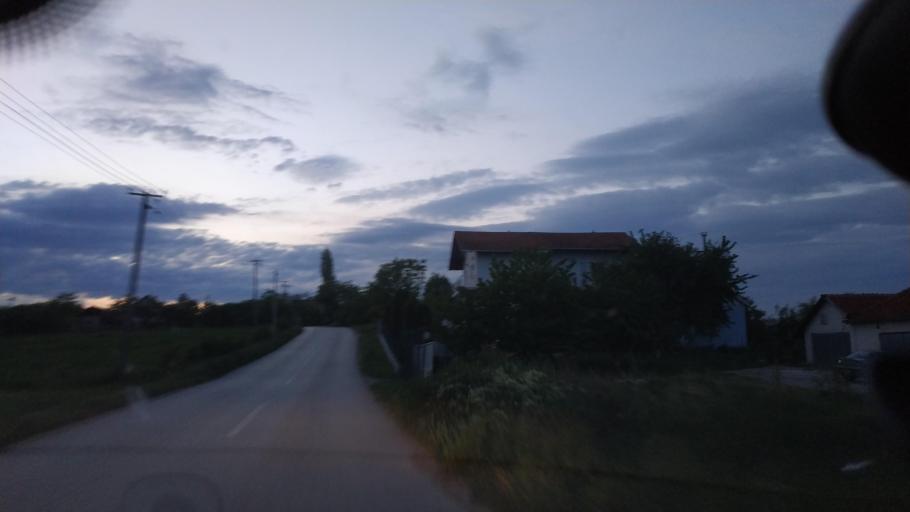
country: RS
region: Central Serbia
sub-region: Nisavski Okrug
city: Merosina
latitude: 43.3042
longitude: 21.6928
